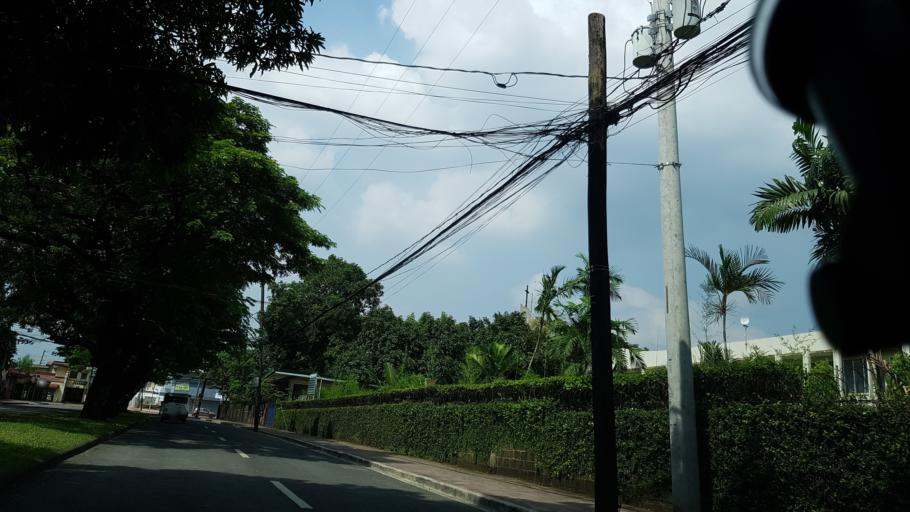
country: PH
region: Calabarzon
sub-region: Province of Rizal
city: Antipolo
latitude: 14.6528
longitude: 121.1161
